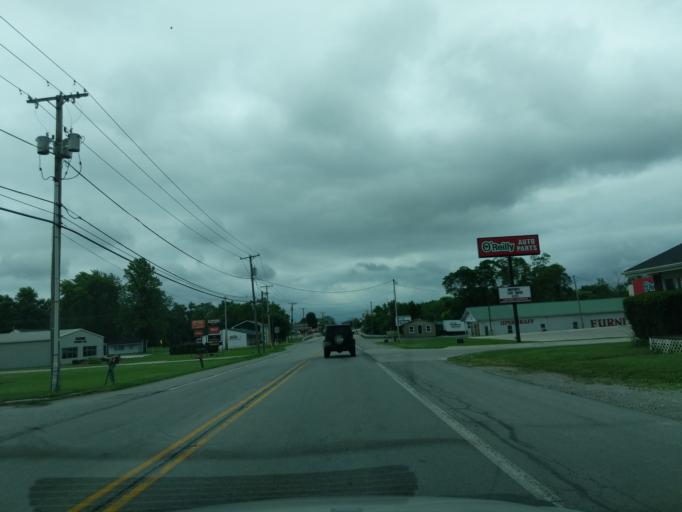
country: US
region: Indiana
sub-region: Madison County
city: Elwood
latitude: 40.2770
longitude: -85.8196
